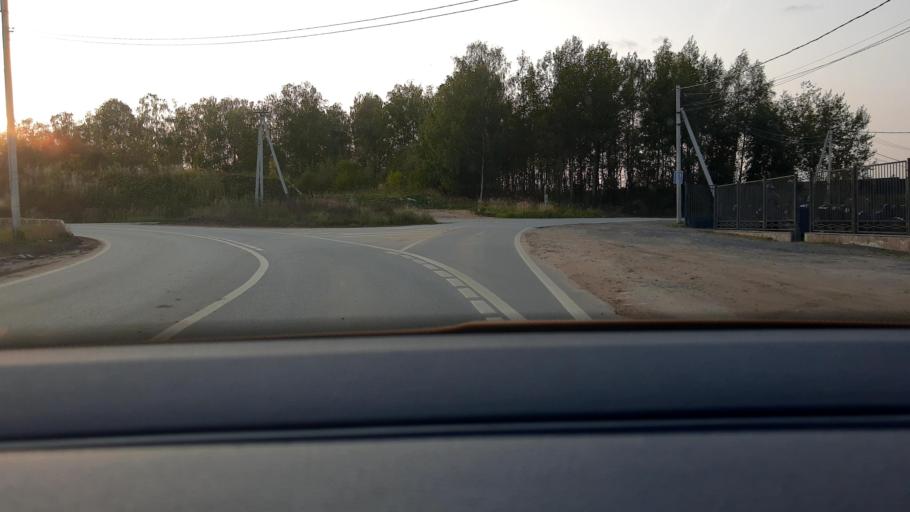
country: RU
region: Moskovskaya
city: Lobnya
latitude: 55.9997
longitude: 37.4014
